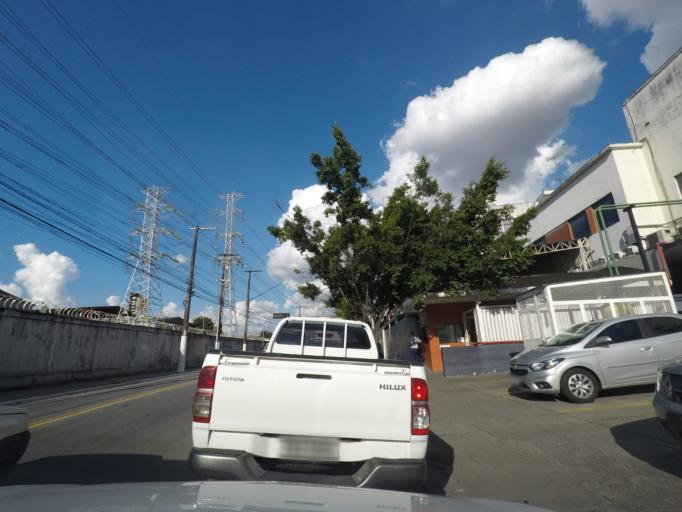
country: BR
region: Sao Paulo
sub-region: Sao Paulo
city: Sao Paulo
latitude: -23.5038
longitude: -46.6753
